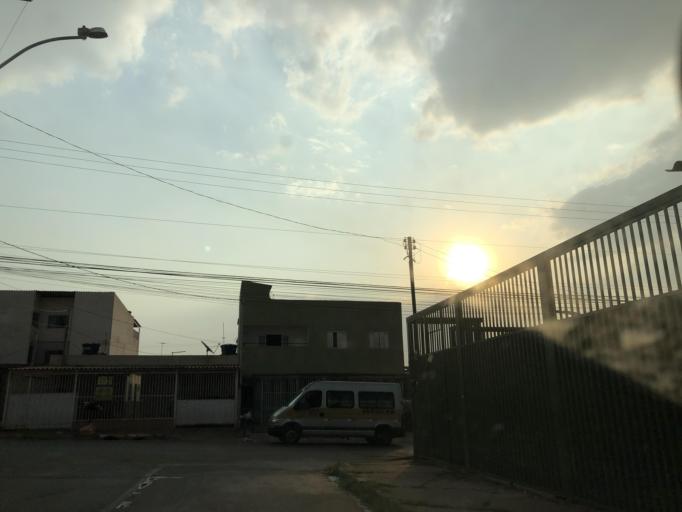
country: BR
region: Federal District
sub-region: Brasilia
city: Brasilia
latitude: -15.9018
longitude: -48.0637
